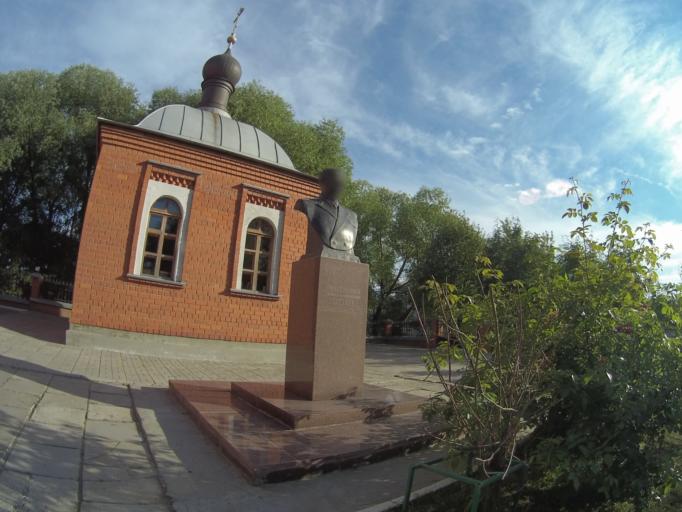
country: RU
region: Vladimir
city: Raduzhnyy
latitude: 56.0996
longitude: 40.2747
